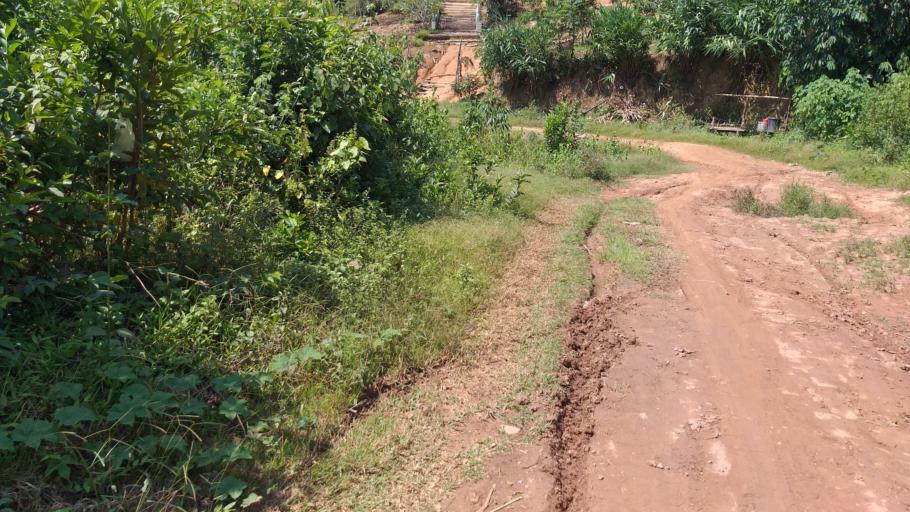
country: LA
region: Phongsali
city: Khoa
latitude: 21.3463
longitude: 102.5388
